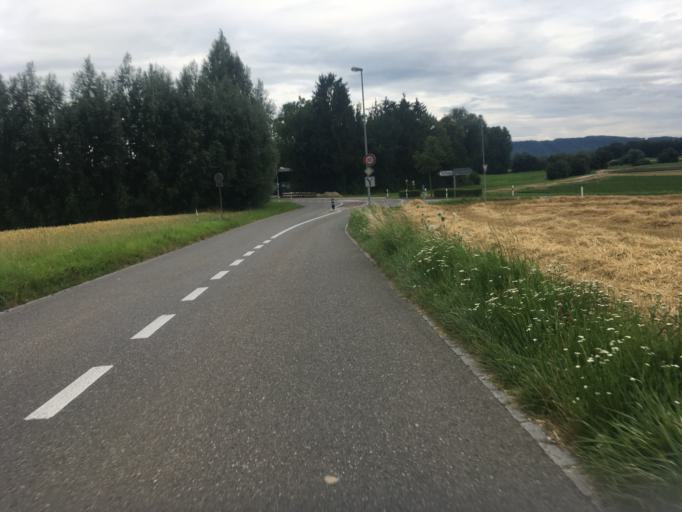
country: CH
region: Bern
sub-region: Seeland District
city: Ins
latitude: 47.0127
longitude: 7.0831
